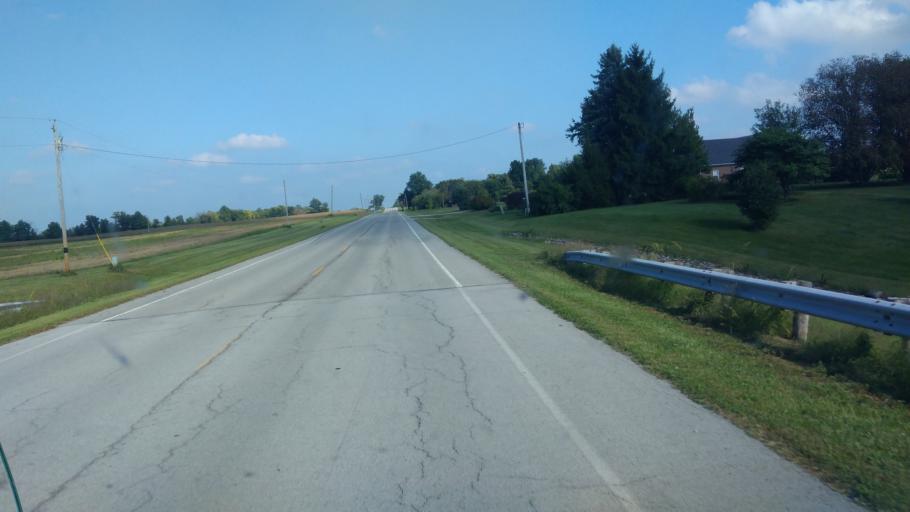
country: US
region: Ohio
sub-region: Hancock County
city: Arlington
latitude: 40.8340
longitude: -83.6649
